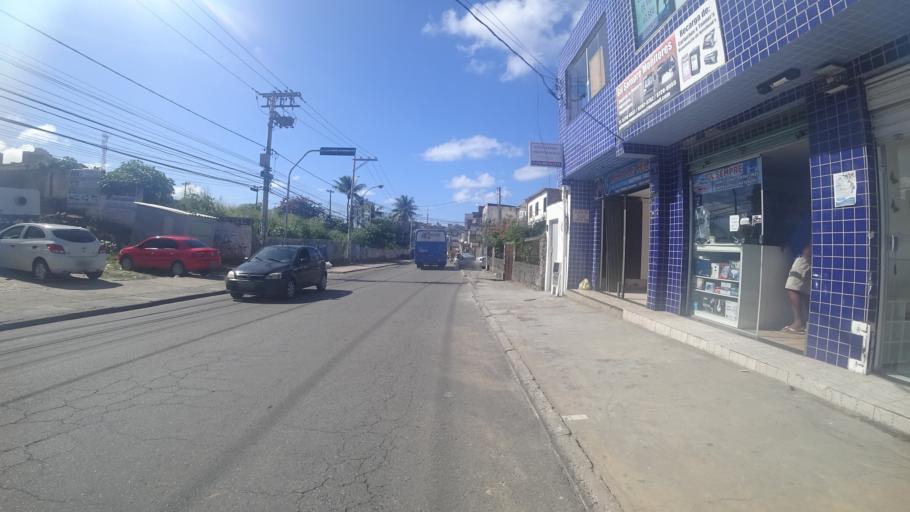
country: BR
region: Bahia
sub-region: Salvador
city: Salvador
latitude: -12.9746
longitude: -38.4331
